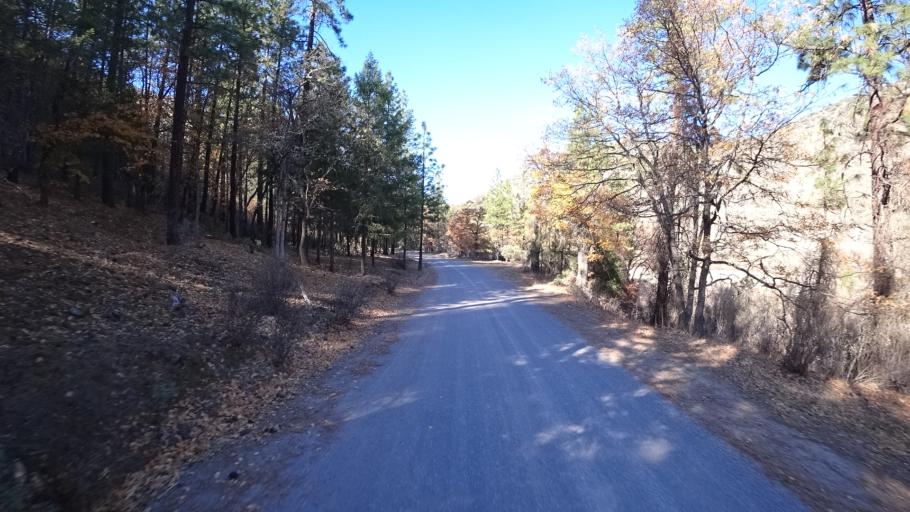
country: US
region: California
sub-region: Siskiyou County
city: Yreka
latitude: 41.8537
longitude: -122.6964
